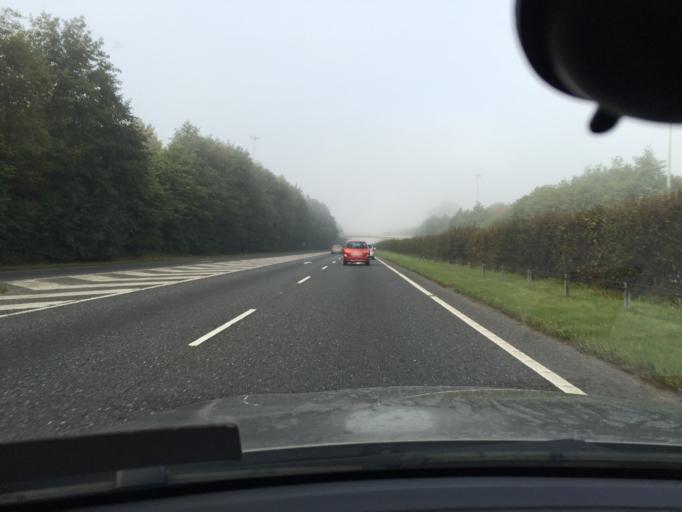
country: IE
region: Leinster
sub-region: Kildare
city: Leixlip
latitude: 53.3583
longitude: -6.4774
